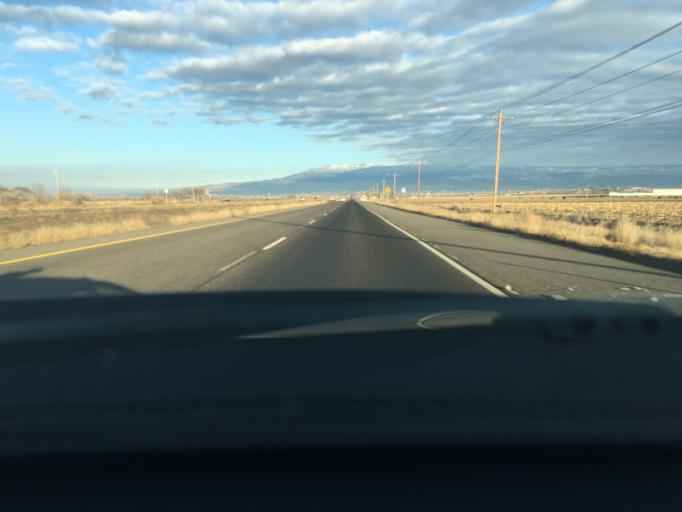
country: US
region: Colorado
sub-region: Montrose County
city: Olathe
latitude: 38.6779
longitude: -108.0055
